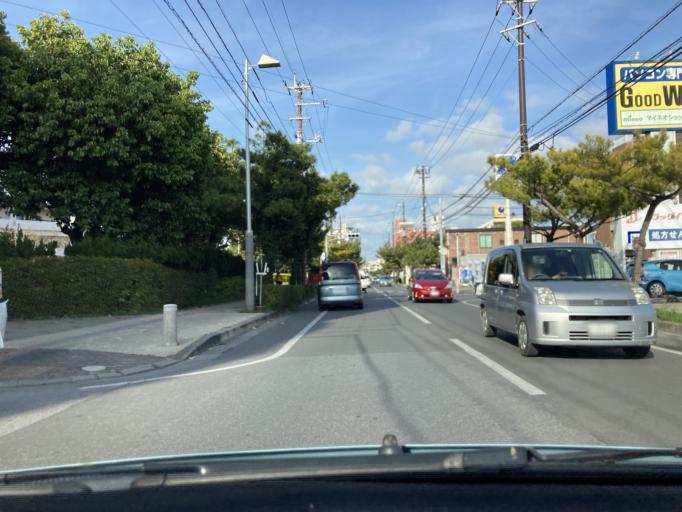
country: JP
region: Okinawa
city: Naha-shi
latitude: 26.2305
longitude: 127.6935
